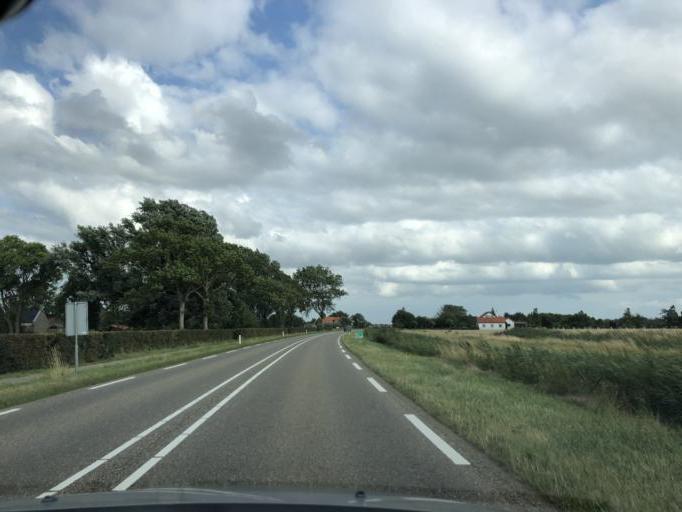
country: NL
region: Zeeland
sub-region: Schouwen-Duiveland
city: Scharendijke
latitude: 51.6880
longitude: 3.8507
